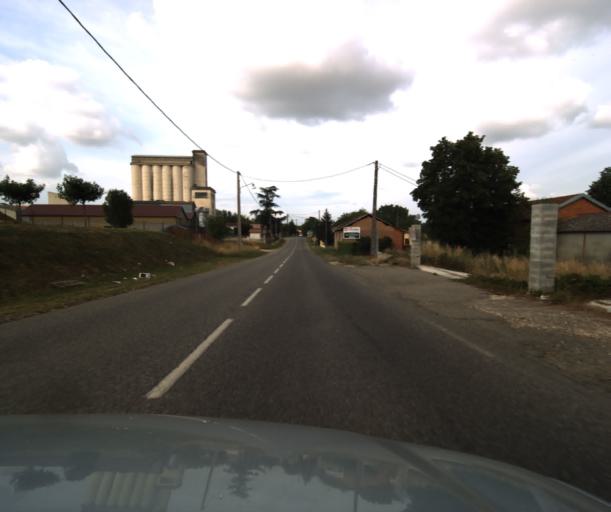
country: FR
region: Midi-Pyrenees
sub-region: Departement du Tarn-et-Garonne
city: Beaumont-de-Lomagne
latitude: 43.8857
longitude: 0.9959
